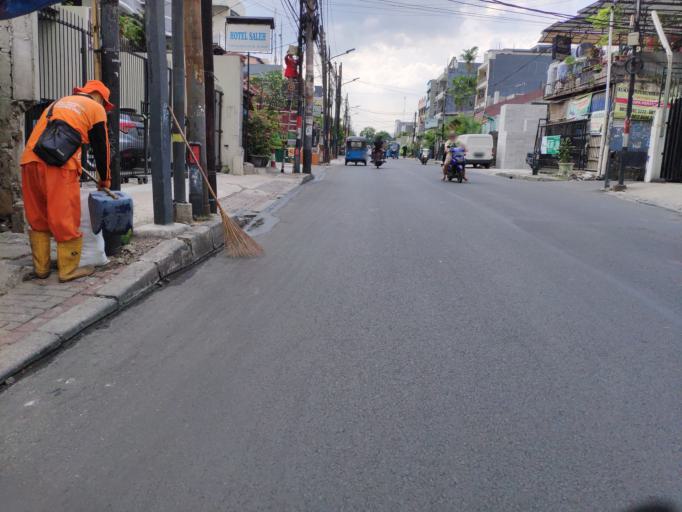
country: ID
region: Jakarta Raya
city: Jakarta
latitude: -6.1937
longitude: 106.8674
